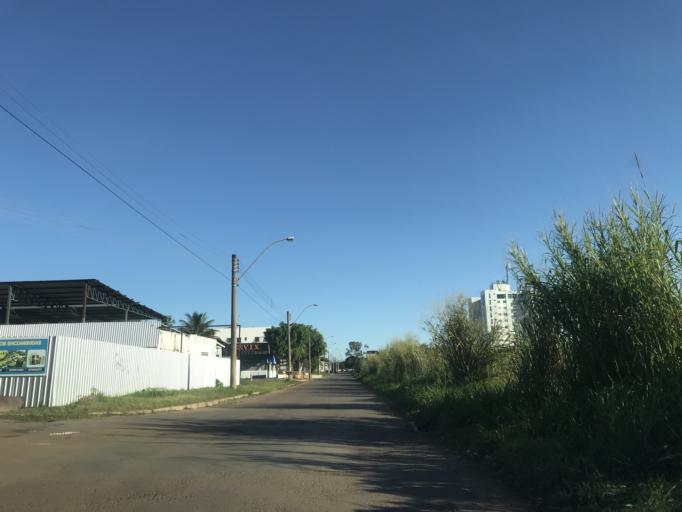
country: BR
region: Federal District
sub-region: Brasilia
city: Brasilia
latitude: -15.8230
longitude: -47.9582
